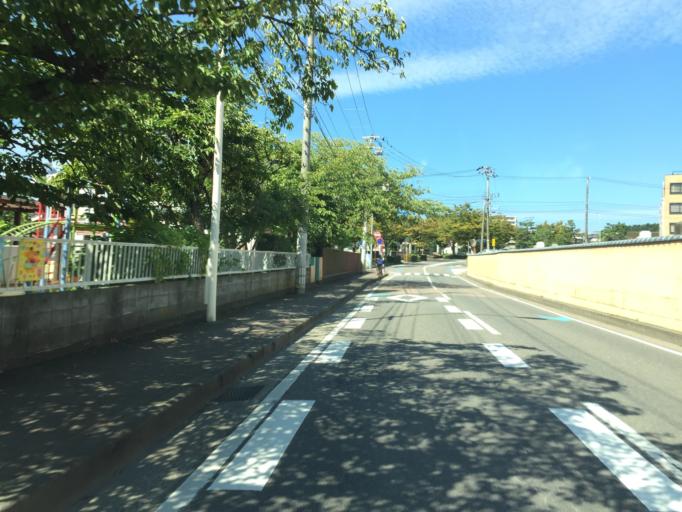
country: JP
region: Niigata
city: Niigata-shi
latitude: 37.9269
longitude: 139.0440
